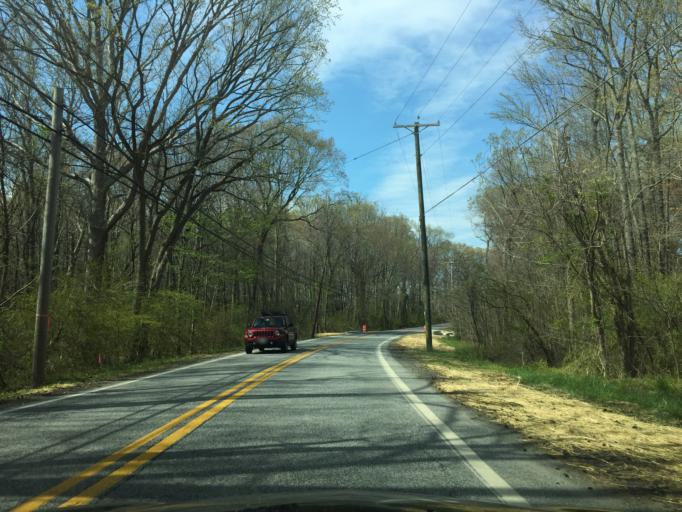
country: US
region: Maryland
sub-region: Baltimore County
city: Edgemere
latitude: 39.2715
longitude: -76.4262
